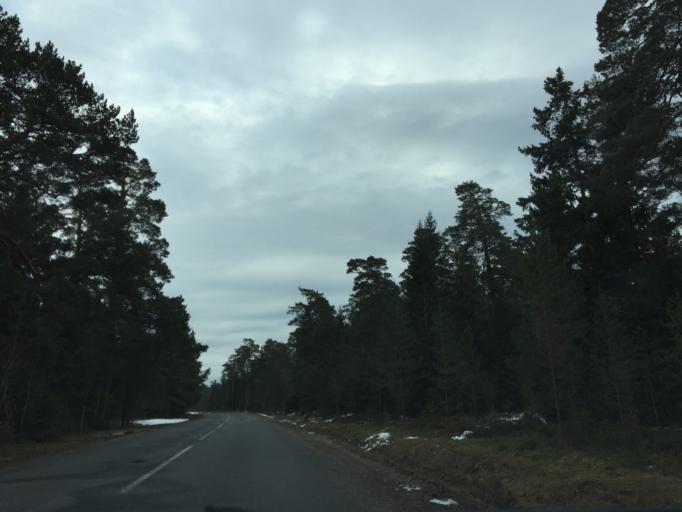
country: EE
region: Saare
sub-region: Kuressaare linn
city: Kuressaare
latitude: 58.4331
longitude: 22.0679
